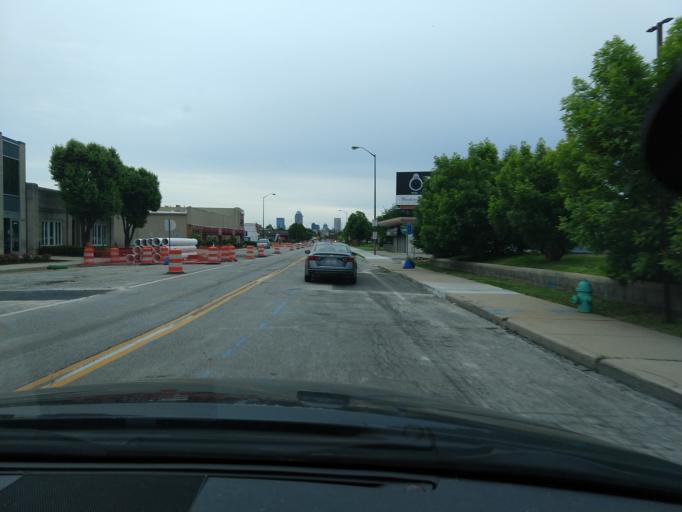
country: US
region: Indiana
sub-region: Marion County
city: Indianapolis
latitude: 39.8026
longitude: -86.1568
